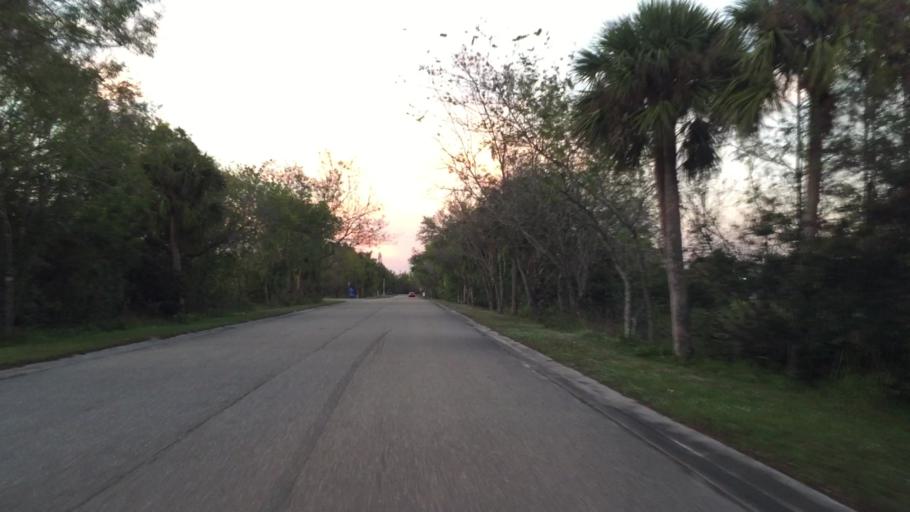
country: US
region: Florida
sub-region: Lee County
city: Gateway
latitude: 26.5347
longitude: -81.7915
